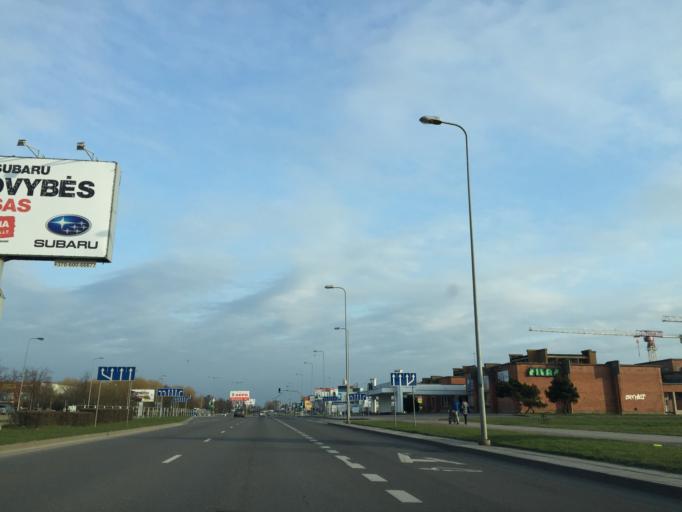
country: LT
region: Klaipedos apskritis
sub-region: Klaipeda
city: Klaipeda
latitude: 55.6909
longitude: 21.1540
